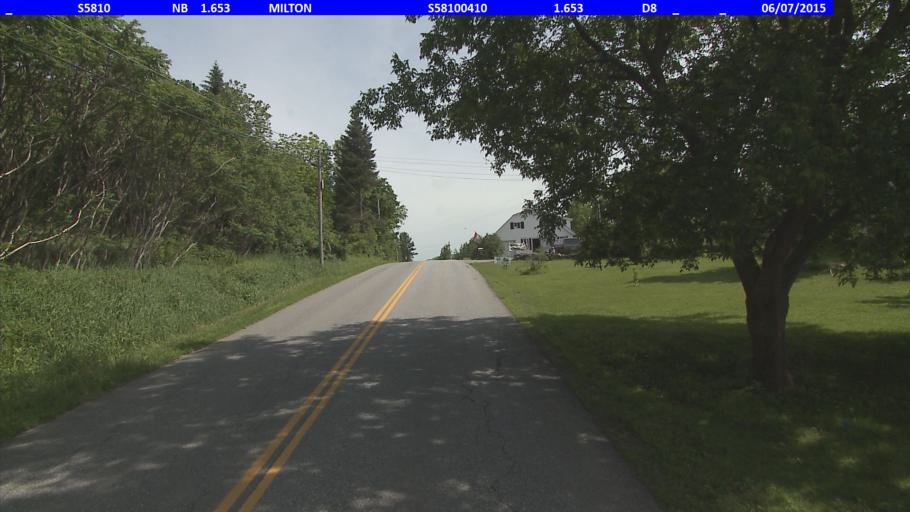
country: US
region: Vermont
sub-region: Chittenden County
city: Milton
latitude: 44.6049
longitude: -73.1250
